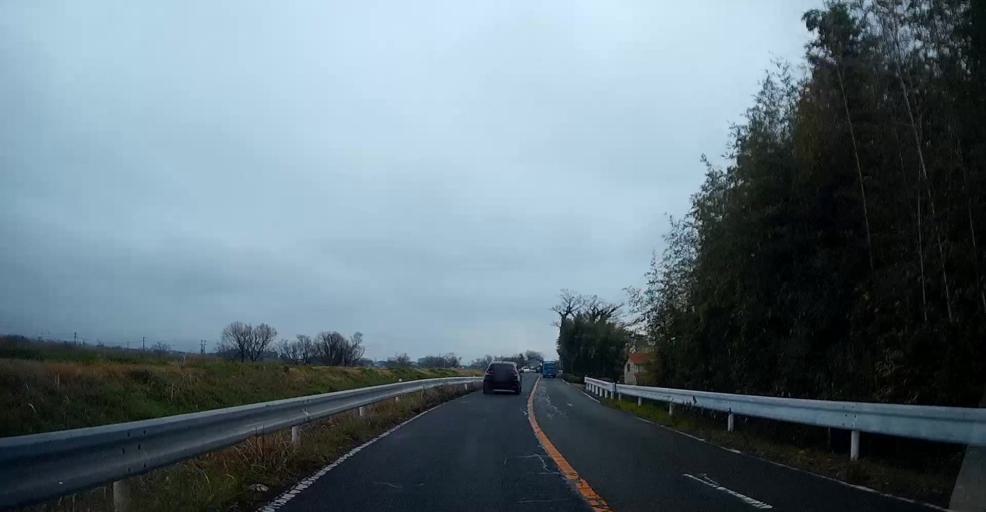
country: JP
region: Kumamoto
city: Kumamoto
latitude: 32.7551
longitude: 130.7481
